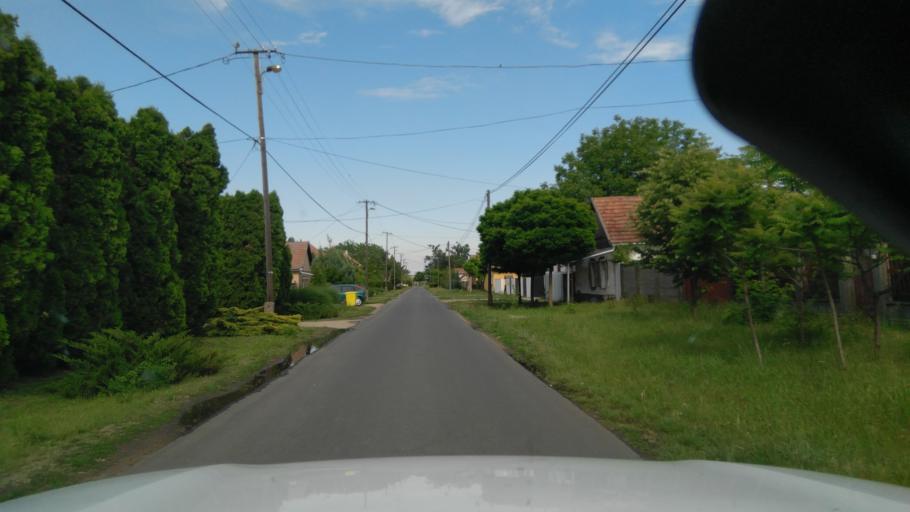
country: HU
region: Bekes
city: Ujkigyos
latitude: 46.5831
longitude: 21.0366
